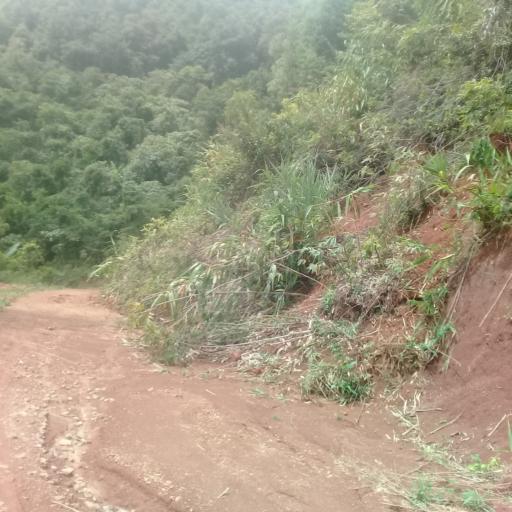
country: VN
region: Huyen Dien Bien
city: Thi Tran Muong Cha
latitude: 21.6634
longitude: 102.9149
